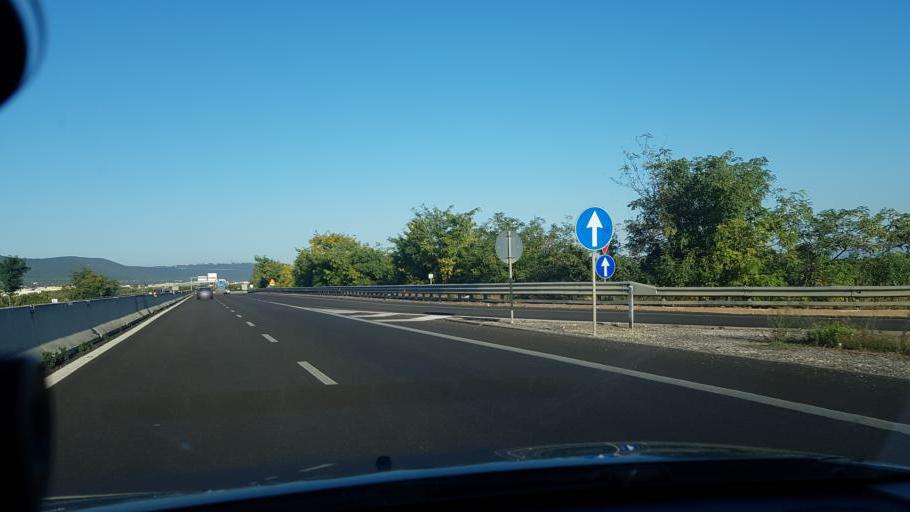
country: IT
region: Apulia
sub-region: Provincia di Brindisi
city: Fasano
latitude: 40.8409
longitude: 17.3709
